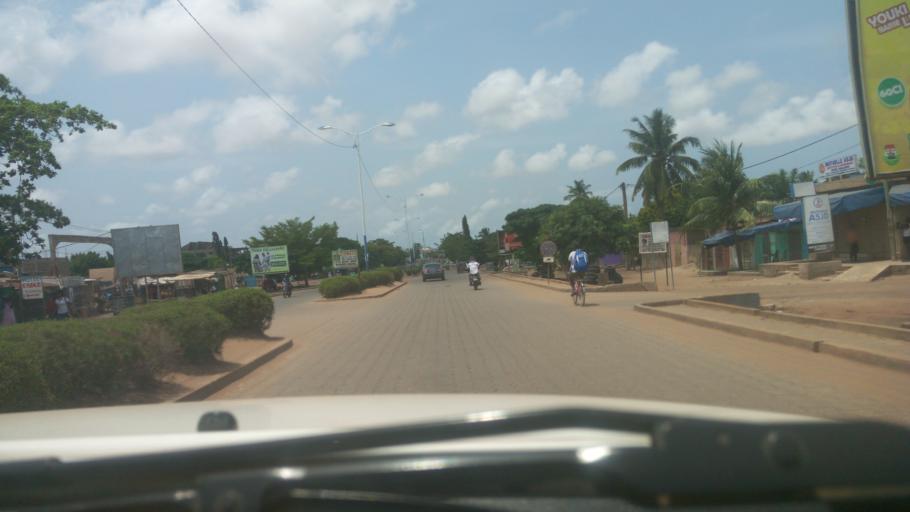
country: TG
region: Maritime
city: Lome
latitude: 6.1978
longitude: 1.2009
